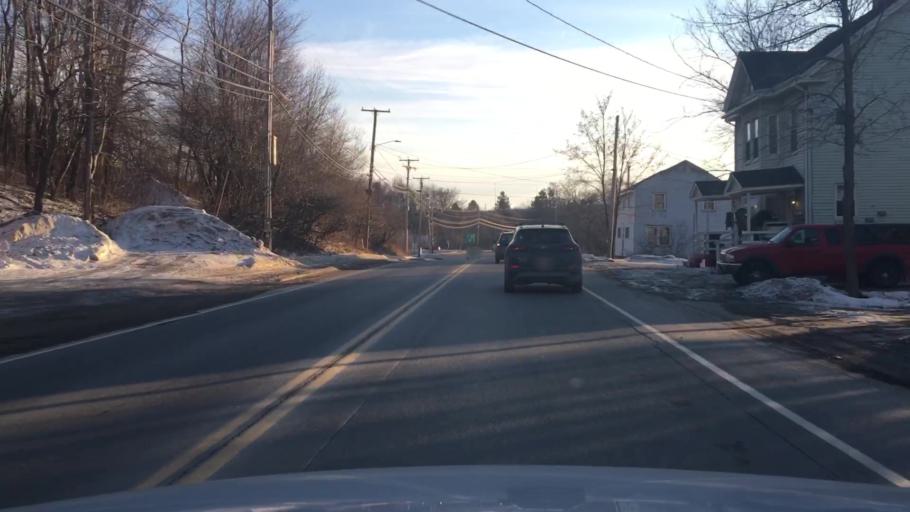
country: US
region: Maine
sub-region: Penobscot County
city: Brewer
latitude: 44.7875
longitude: -68.7707
